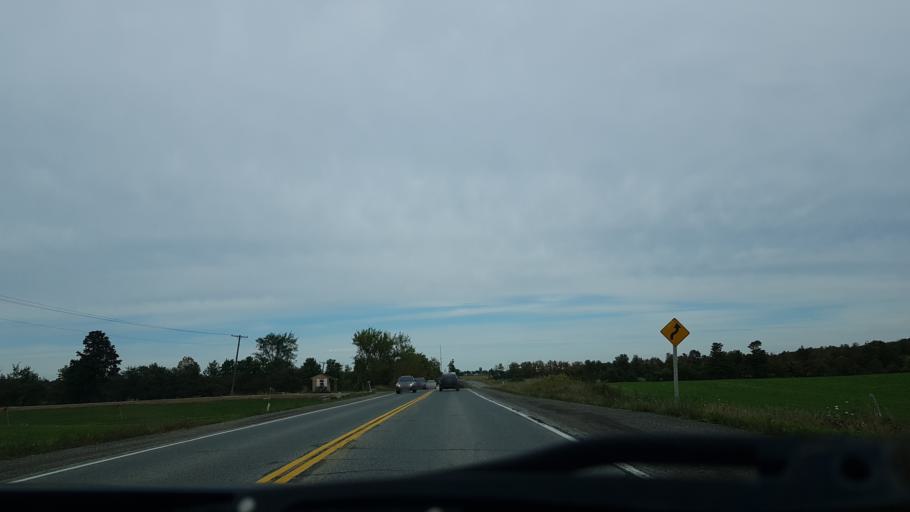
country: CA
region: Ontario
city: Orangeville
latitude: 43.8915
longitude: -79.9609
